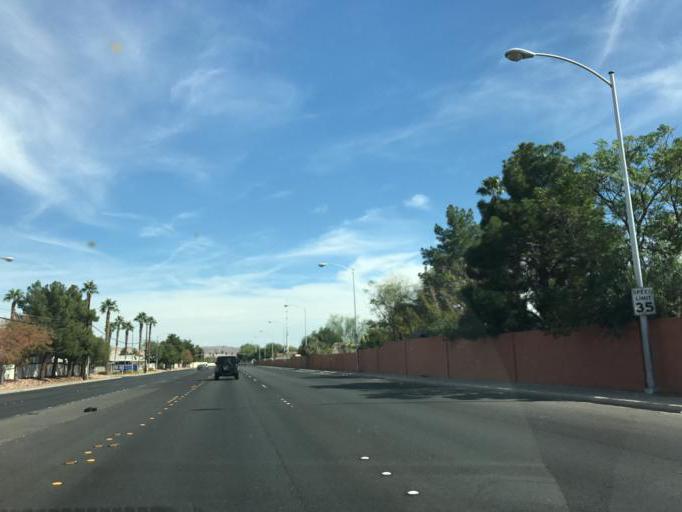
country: US
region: Nevada
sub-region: Clark County
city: Winchester
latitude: 36.1297
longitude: -115.0601
